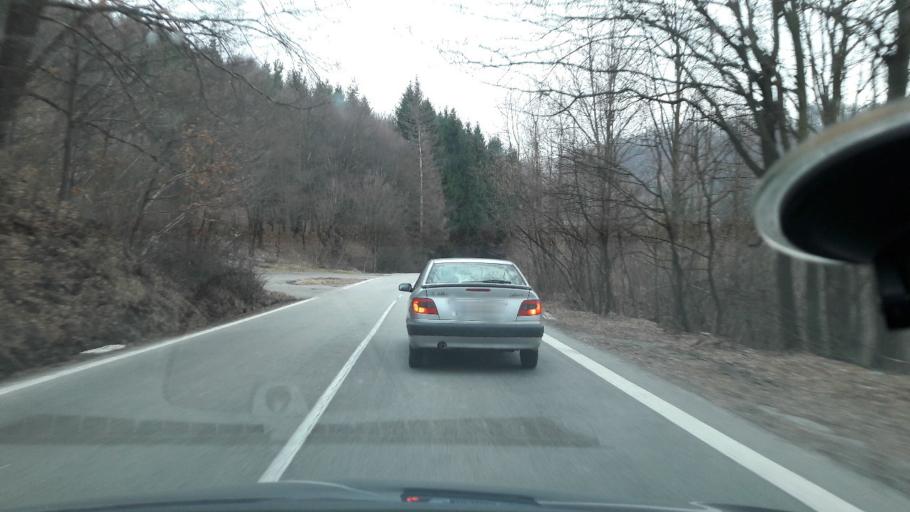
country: SK
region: Nitriansky
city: Handlova
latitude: 48.6689
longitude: 18.7314
